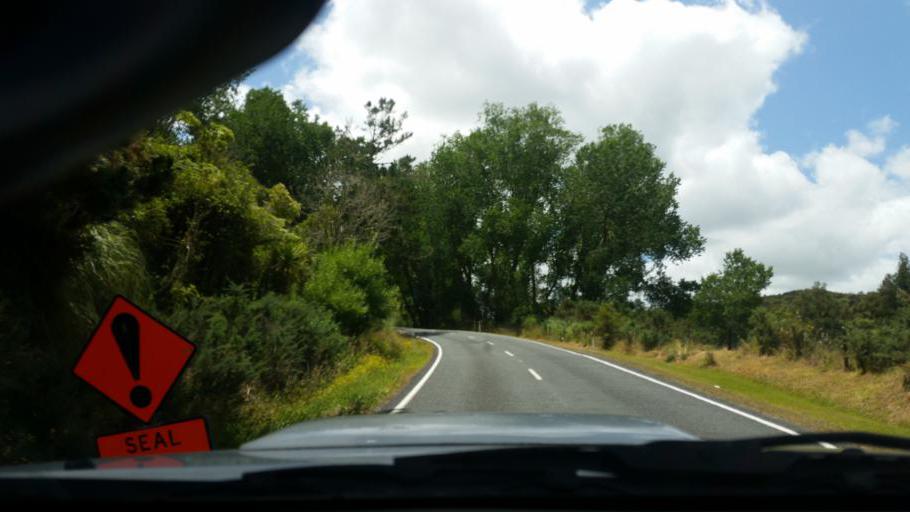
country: NZ
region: Northland
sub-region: Whangarei
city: Ruakaka
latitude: -36.0937
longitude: 174.2433
